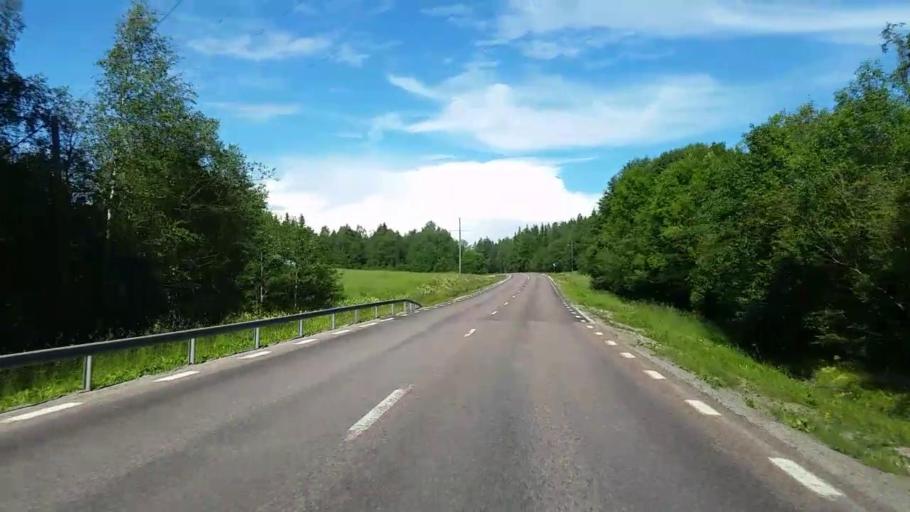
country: SE
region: Dalarna
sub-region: Rattviks Kommun
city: Raettvik
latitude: 61.0233
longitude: 15.2096
